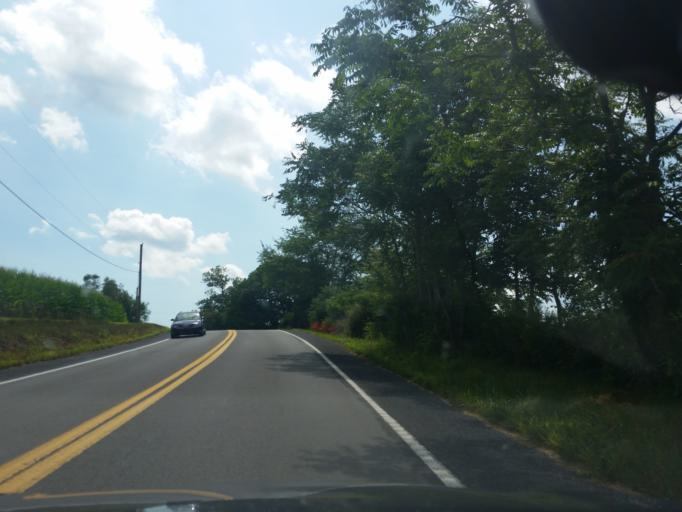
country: US
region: Pennsylvania
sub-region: Dauphin County
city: Elizabethville
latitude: 40.5104
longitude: -76.8760
